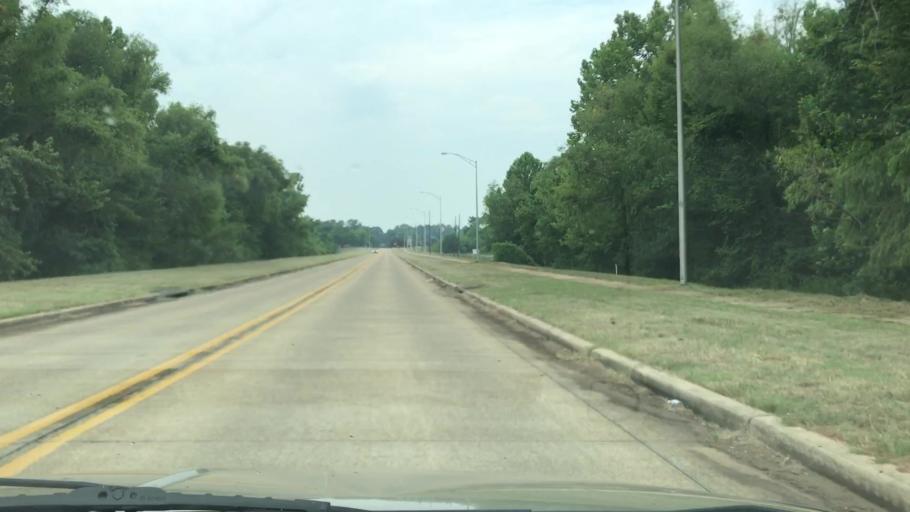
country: US
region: Louisiana
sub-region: Bossier Parish
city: Bossier City
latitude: 32.4712
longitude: -93.7014
